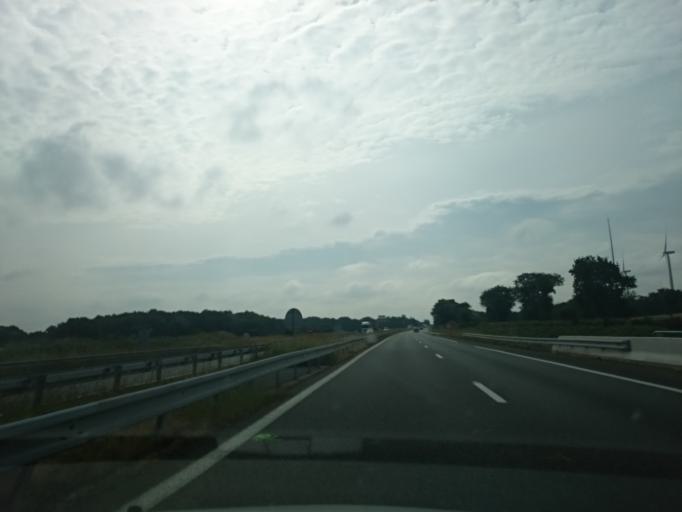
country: FR
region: Brittany
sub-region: Departement du Morbihan
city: Ambon
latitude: 47.5893
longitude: -2.5506
